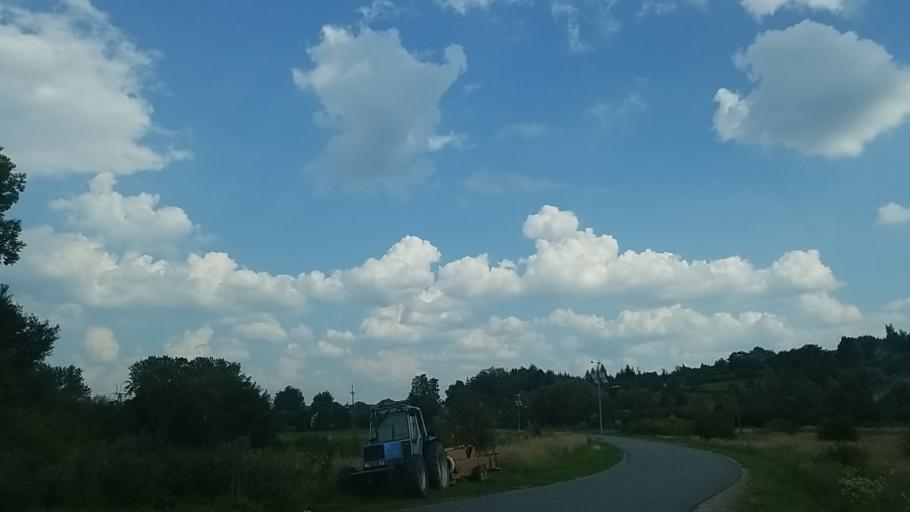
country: PL
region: Lublin Voivodeship
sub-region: Powiat bilgorajski
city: Goraj
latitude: 50.7248
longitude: 22.6538
